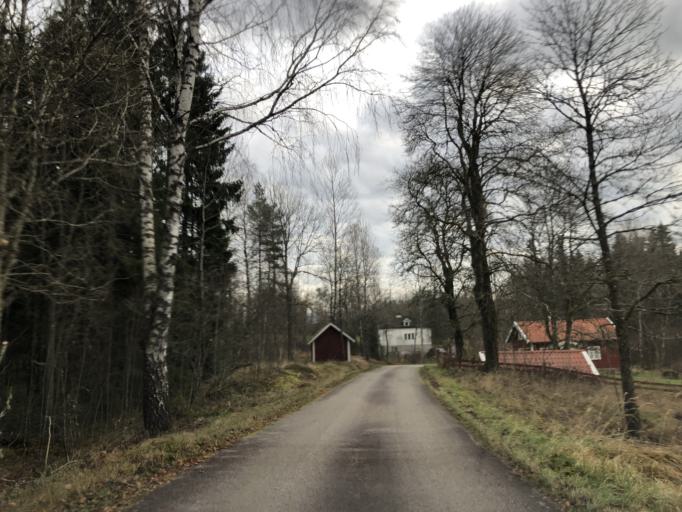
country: SE
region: Vaestra Goetaland
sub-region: Ulricehamns Kommun
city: Ulricehamn
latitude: 57.7272
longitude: 13.3280
